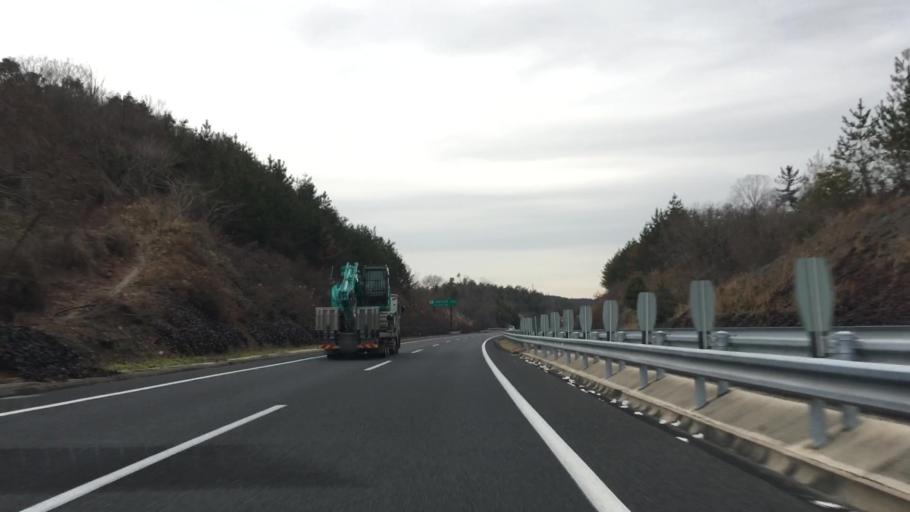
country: JP
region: Gifu
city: Toki
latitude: 35.3118
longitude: 137.1777
